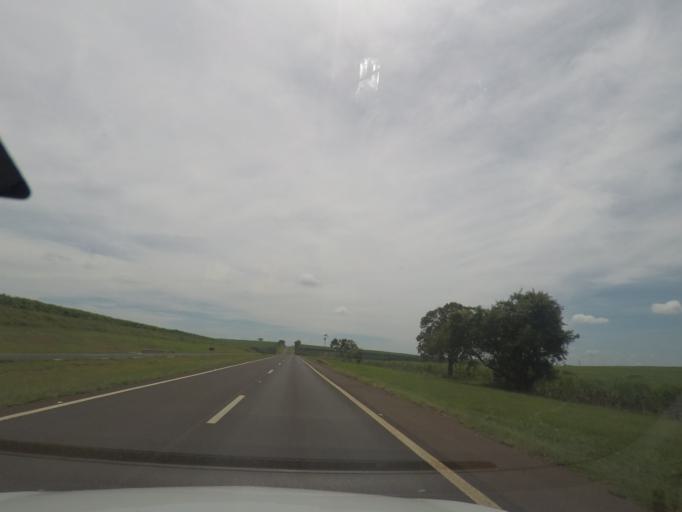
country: BR
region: Sao Paulo
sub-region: Bebedouro
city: Bebedouro
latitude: -21.0354
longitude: -48.4191
